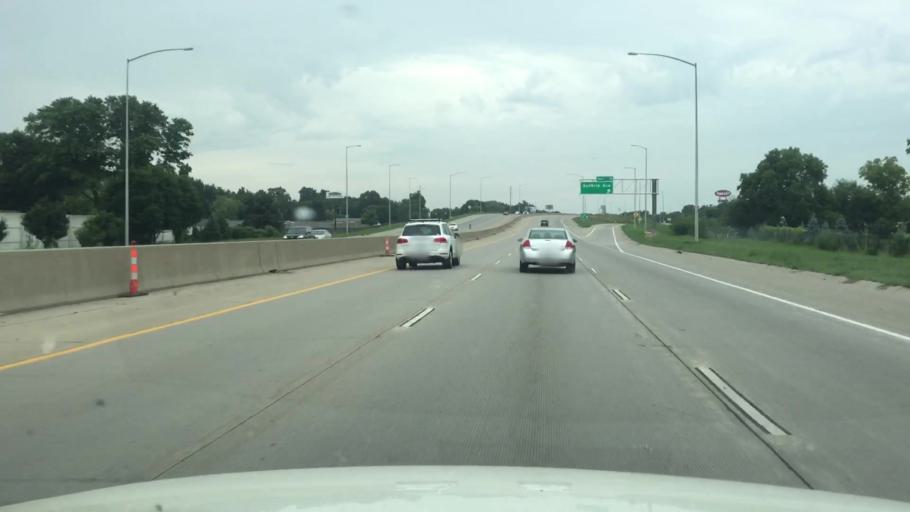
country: US
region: Iowa
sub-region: Polk County
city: Des Moines
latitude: 41.6198
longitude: -93.5766
